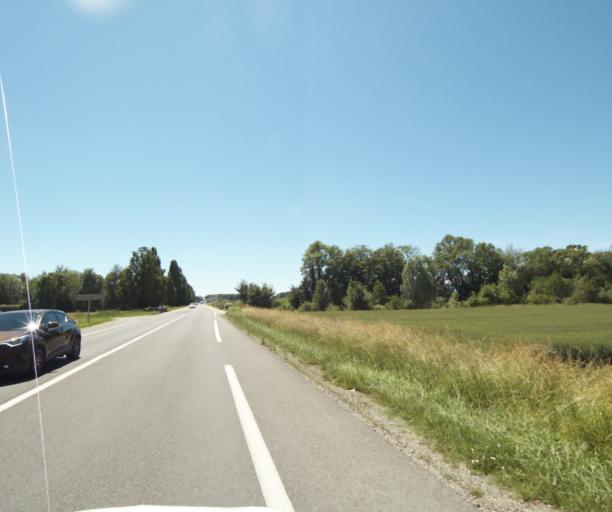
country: FR
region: Rhone-Alpes
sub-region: Departement de la Haute-Savoie
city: Veigy-Foncenex
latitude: 46.2734
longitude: 6.2433
